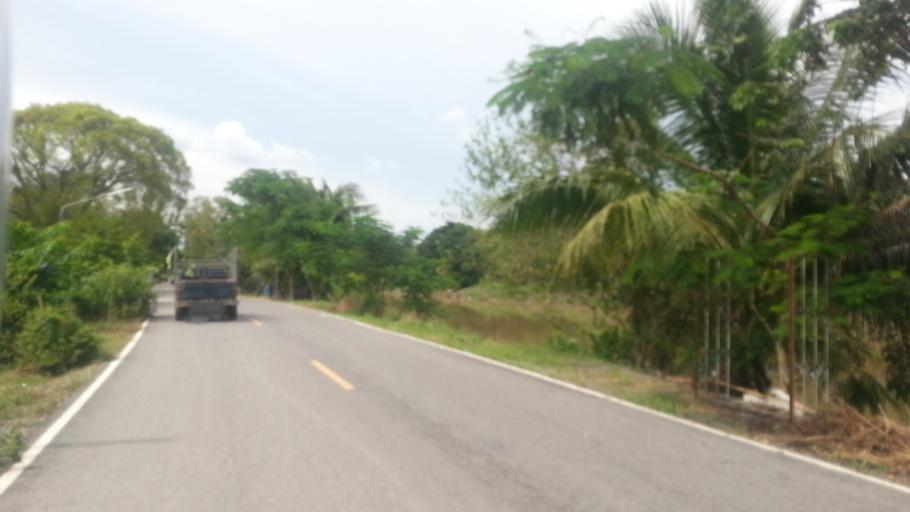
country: TH
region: Pathum Thani
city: Nong Suea
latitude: 14.0804
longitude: 100.8237
